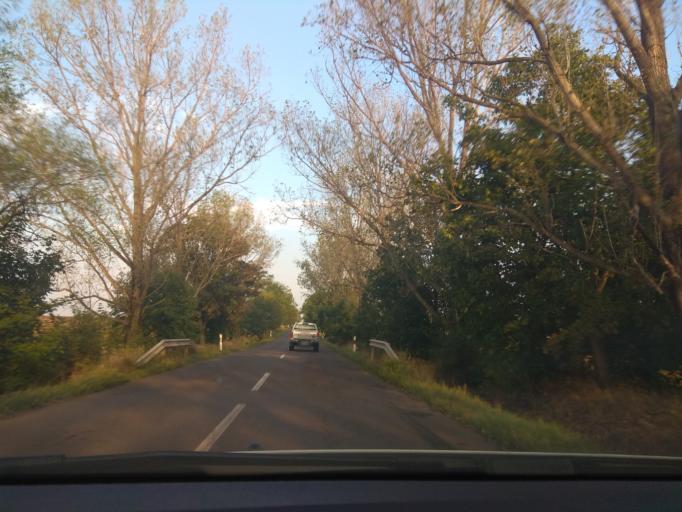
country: HU
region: Heves
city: Ostoros
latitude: 47.8281
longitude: 20.4621
